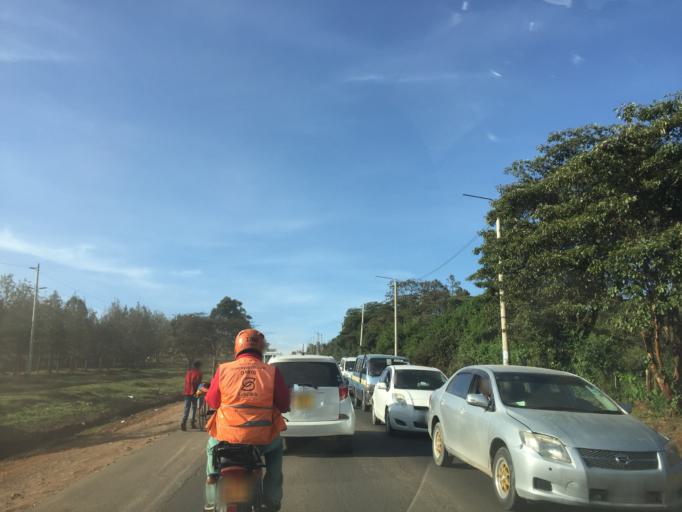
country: KE
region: Nairobi Area
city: Nairobi
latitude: -1.3788
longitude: 36.7701
